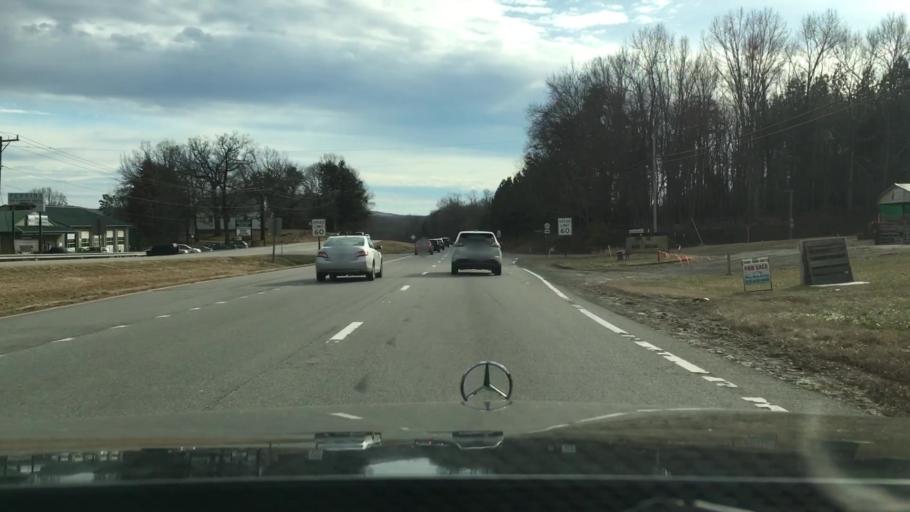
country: US
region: Virginia
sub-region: Pittsylvania County
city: Chatham
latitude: 36.7860
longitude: -79.3942
